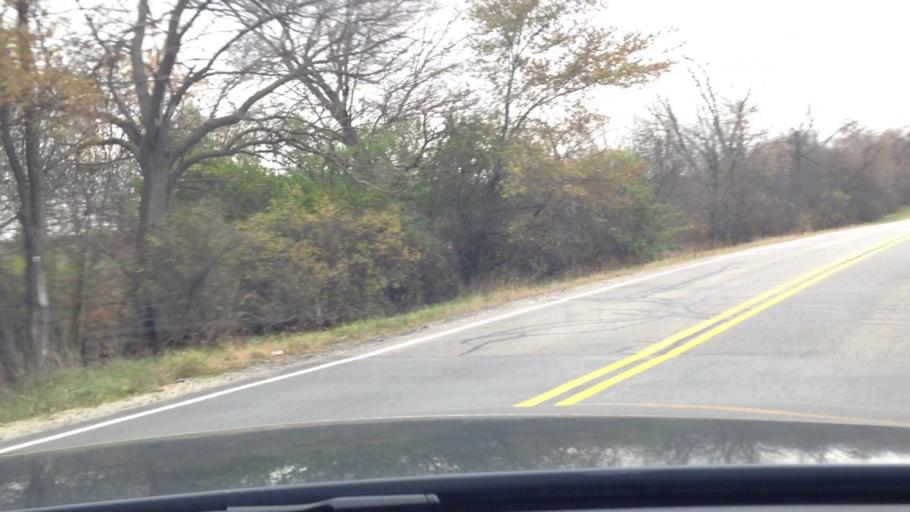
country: US
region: Illinois
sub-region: McHenry County
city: Woodstock
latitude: 42.2766
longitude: -88.4526
